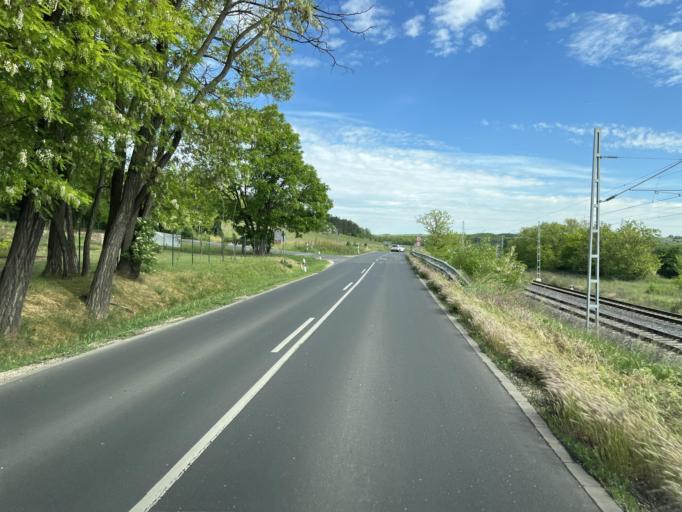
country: HU
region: Pest
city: Isaszeg
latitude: 47.5187
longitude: 19.3672
